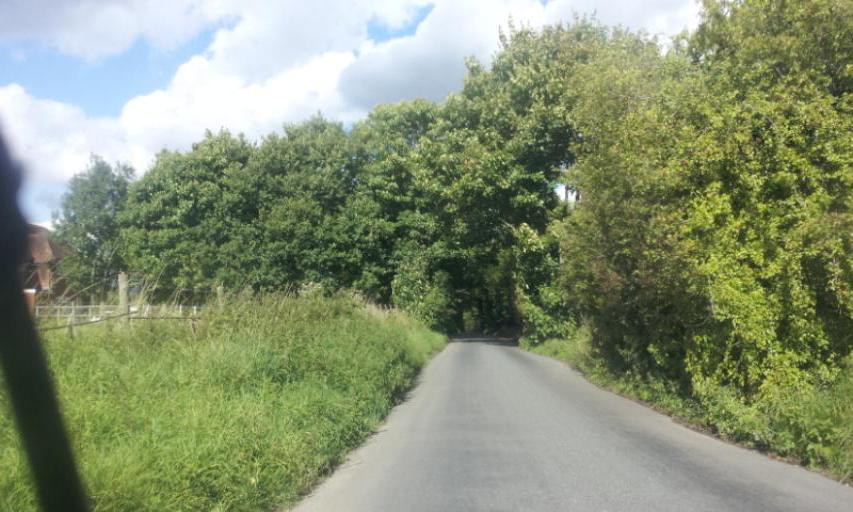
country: GB
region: England
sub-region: Kent
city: West Malling
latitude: 51.3054
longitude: 0.4141
